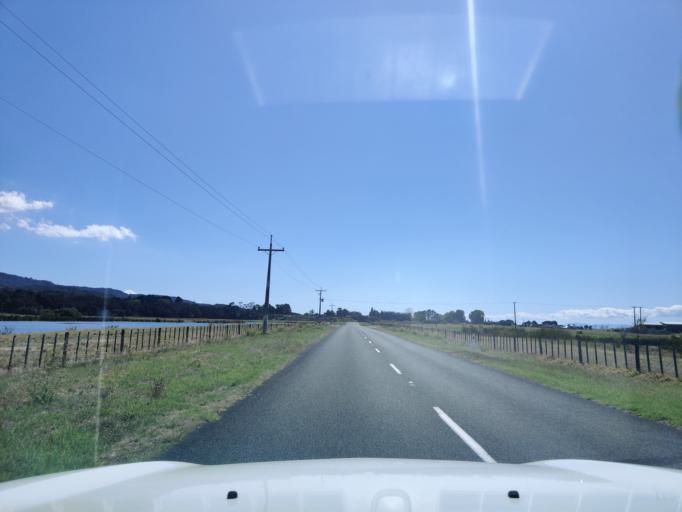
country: NZ
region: Waikato
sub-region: Thames-Coromandel District
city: Thames
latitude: -37.0632
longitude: 175.2984
